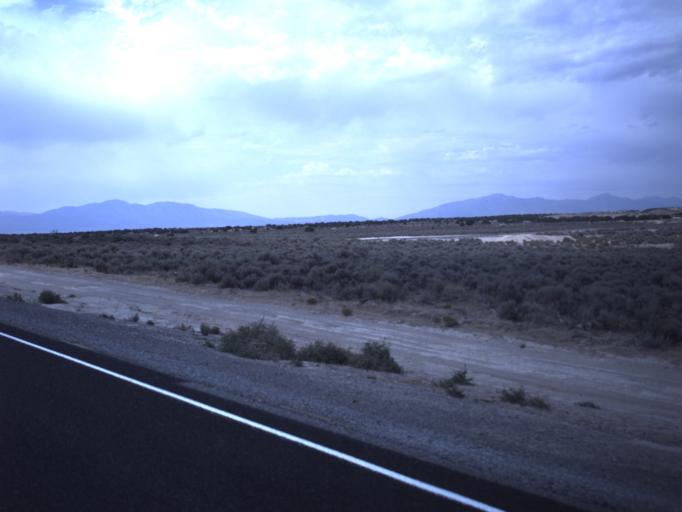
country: US
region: Utah
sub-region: Utah County
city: Eagle Mountain
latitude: 40.2319
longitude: -112.1767
